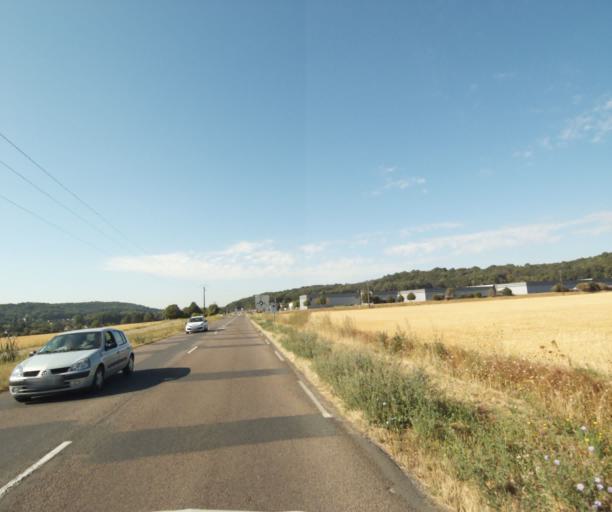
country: FR
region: Ile-de-France
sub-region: Departement de l'Essonne
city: Baulne
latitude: 48.5025
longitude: 2.3529
